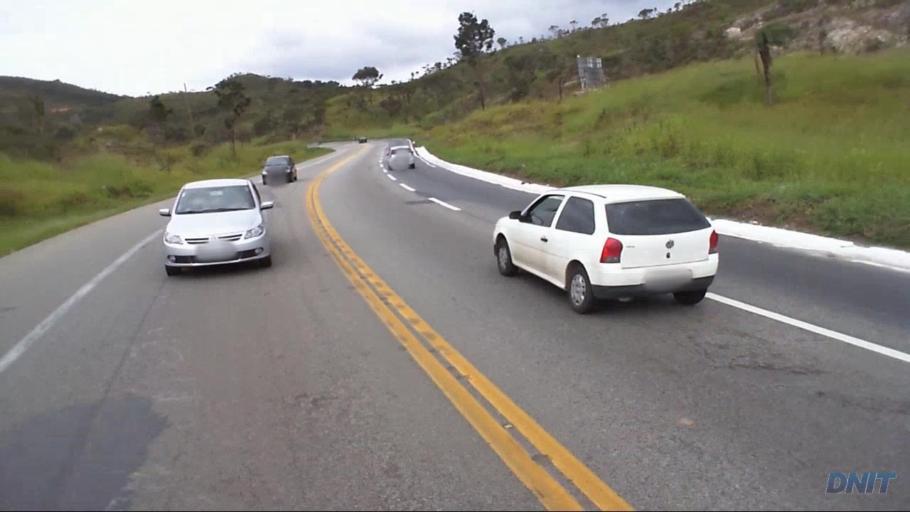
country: BR
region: Minas Gerais
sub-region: Caete
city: Caete
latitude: -19.7863
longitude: -43.7109
